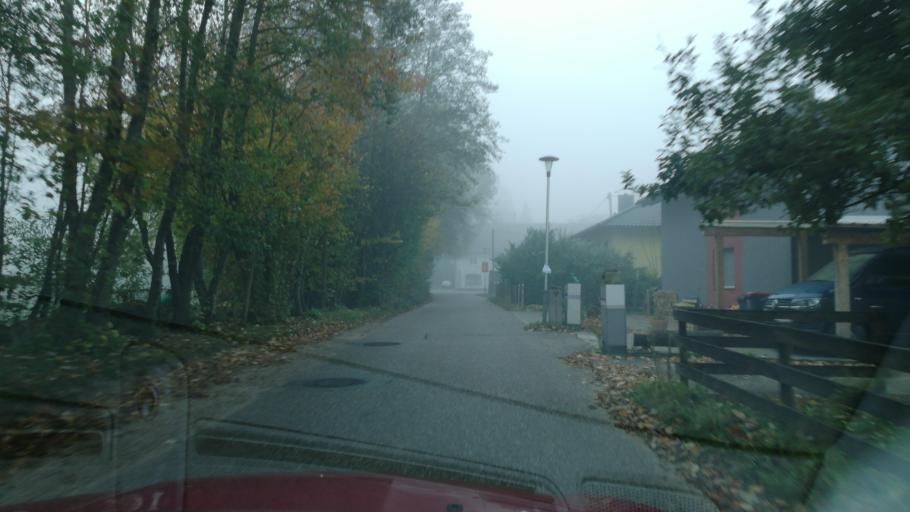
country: AT
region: Upper Austria
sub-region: Politischer Bezirk Grieskirchen
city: Bad Schallerbach
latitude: 48.2177
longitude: 13.8797
